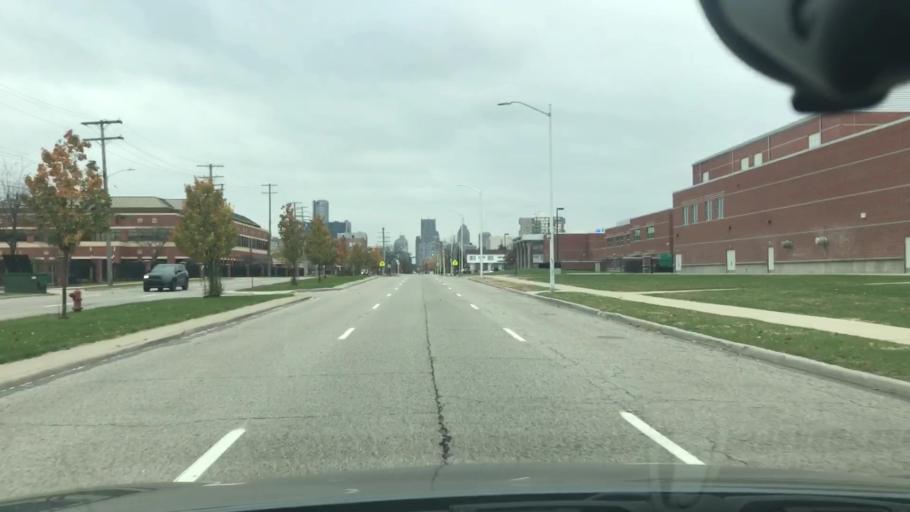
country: US
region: Michigan
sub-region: Wayne County
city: Detroit
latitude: 42.3430
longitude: -83.0142
